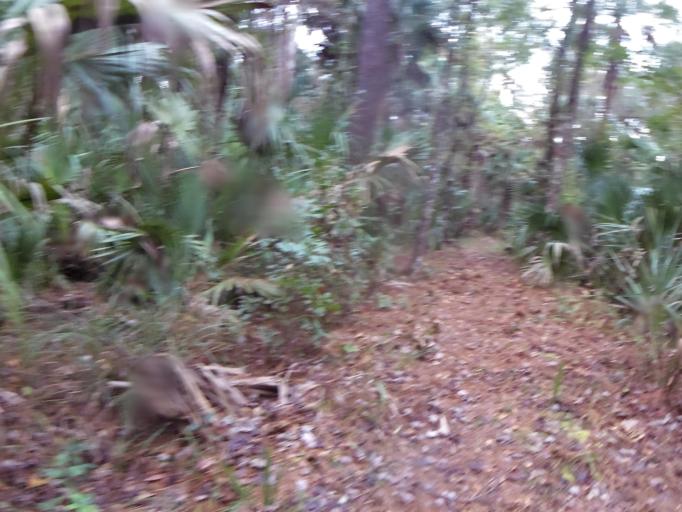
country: US
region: Florida
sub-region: Putnam County
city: Palatka
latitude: 29.6736
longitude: -81.7580
